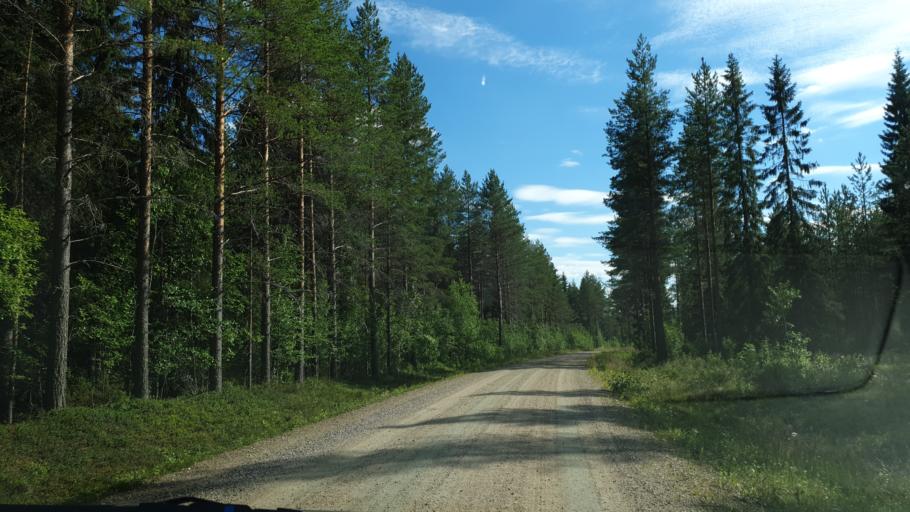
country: FI
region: Kainuu
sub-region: Kehys-Kainuu
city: Kuhmo
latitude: 64.1475
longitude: 29.3303
